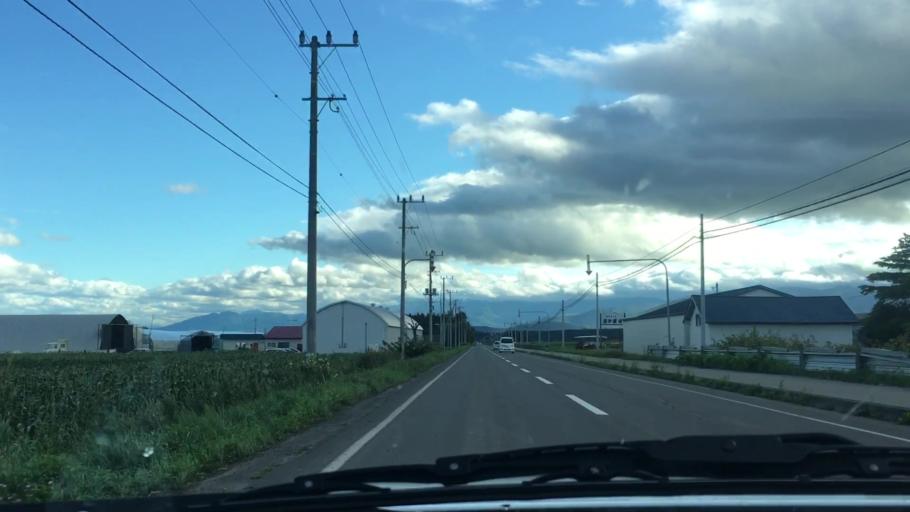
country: JP
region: Hokkaido
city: Otofuke
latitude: 43.1481
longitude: 142.8990
